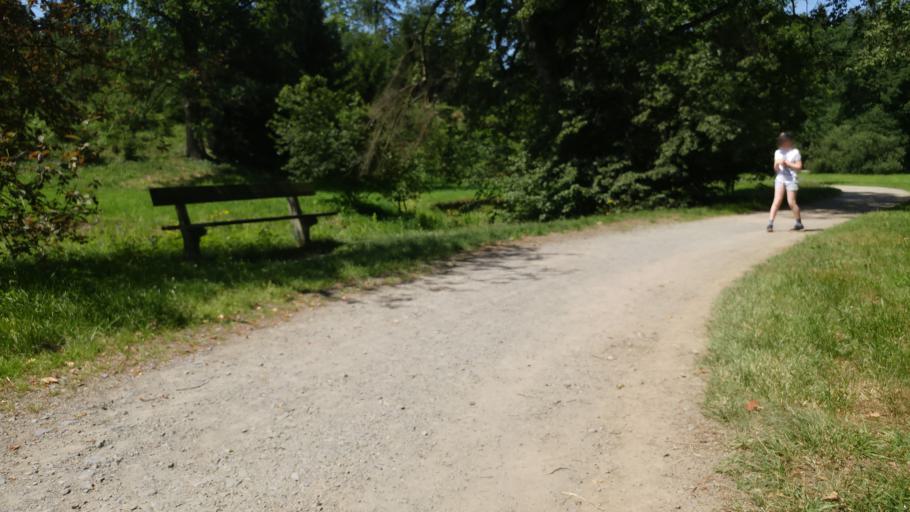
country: CZ
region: Central Bohemia
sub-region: Okres Praha-Zapad
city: Pruhonice
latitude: 49.9911
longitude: 14.5606
